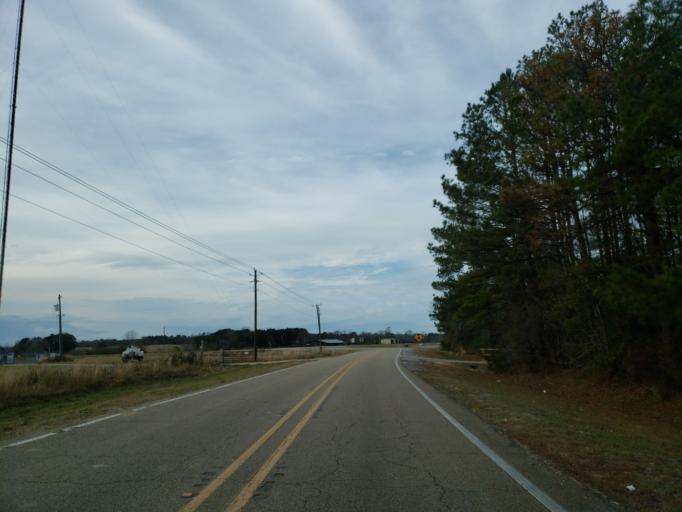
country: US
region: Mississippi
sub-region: Clarke County
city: Quitman
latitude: 31.8783
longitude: -88.7102
